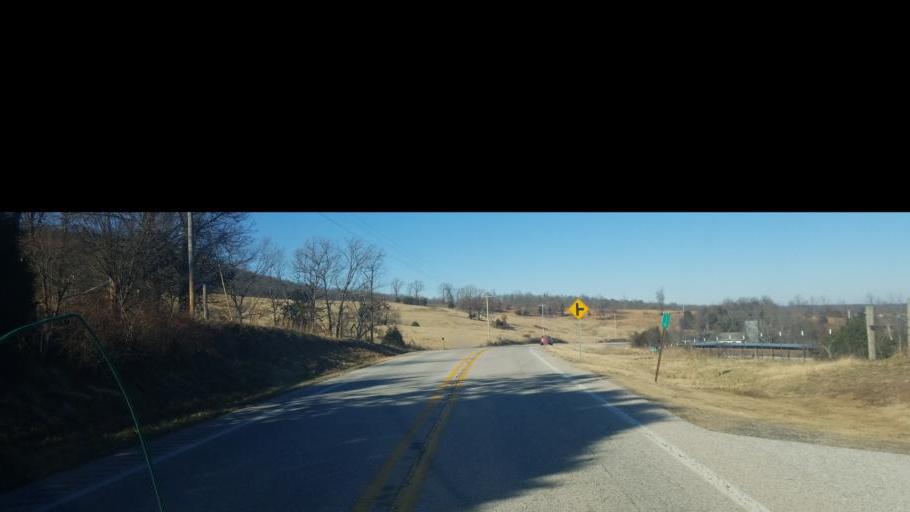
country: US
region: Arkansas
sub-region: Carroll County
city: Green Forest
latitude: 36.2275
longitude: -93.3352
